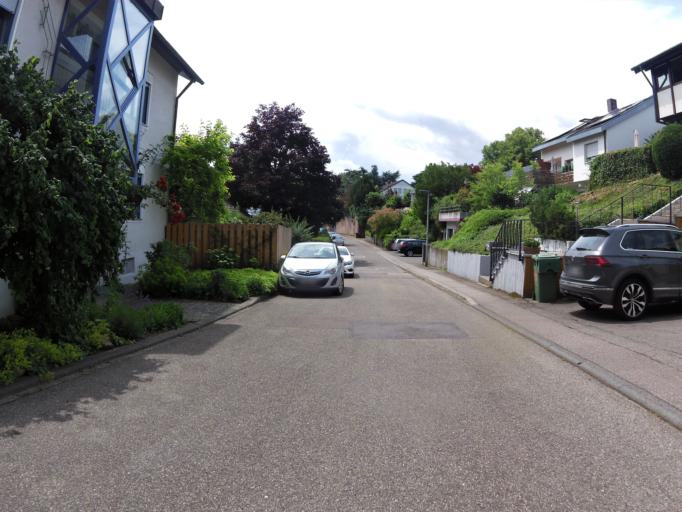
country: DE
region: Baden-Wuerttemberg
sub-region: Freiburg Region
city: Lahr
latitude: 48.3448
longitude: 7.8707
